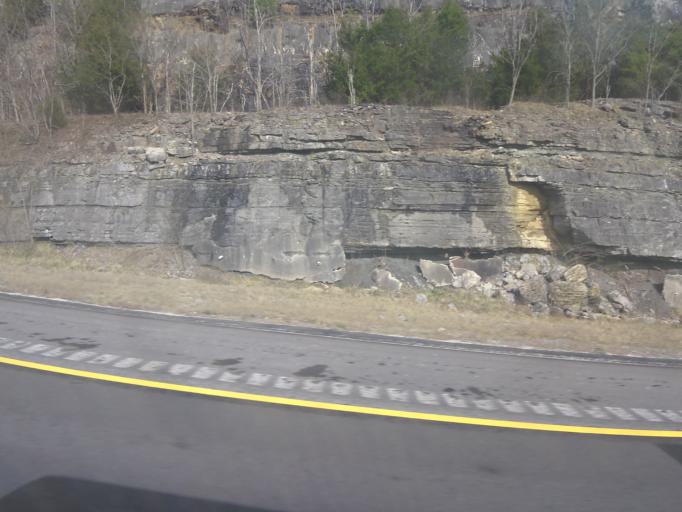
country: US
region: Tennessee
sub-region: Marion County
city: Monteagle
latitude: 35.2070
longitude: -85.8184
